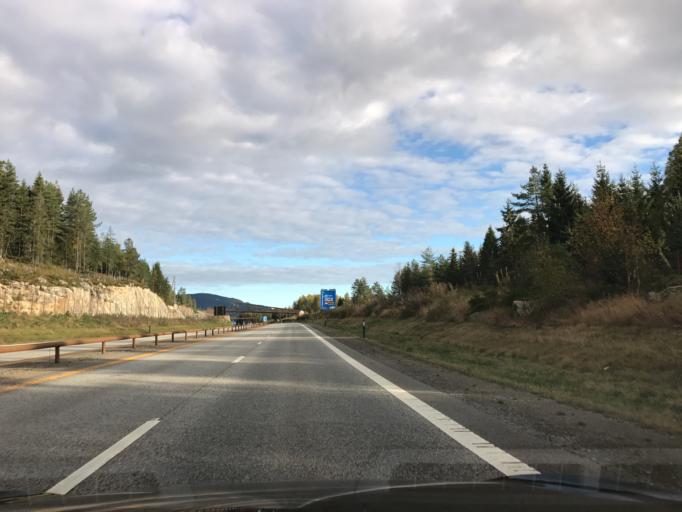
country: NO
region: Akershus
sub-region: Eidsvoll
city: Raholt
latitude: 60.3019
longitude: 11.1396
